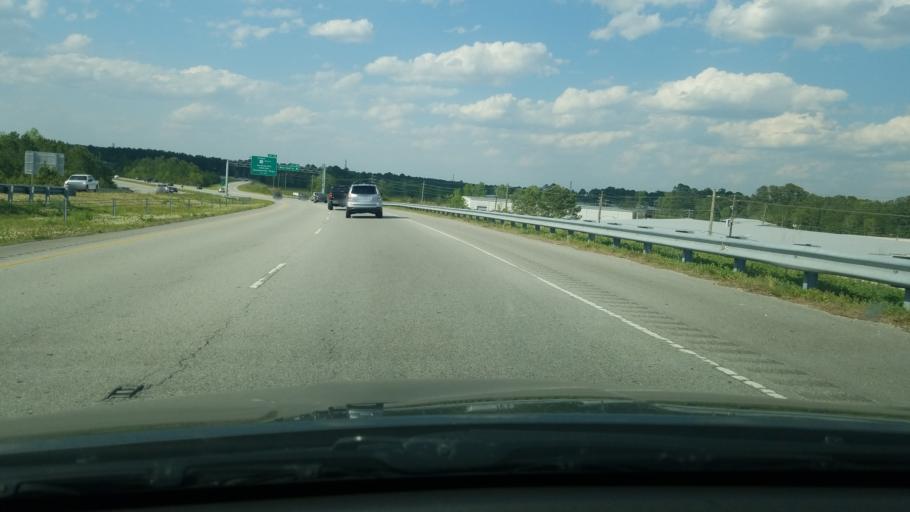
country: US
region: North Carolina
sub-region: Onslow County
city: Jacksonville
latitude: 34.7551
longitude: -77.3956
